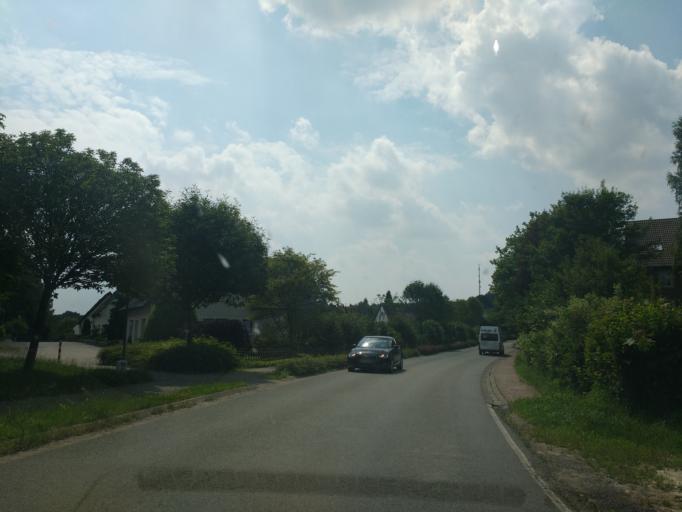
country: DE
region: North Rhine-Westphalia
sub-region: Regierungsbezirk Detmold
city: Dorentrup
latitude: 52.0416
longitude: 9.0081
